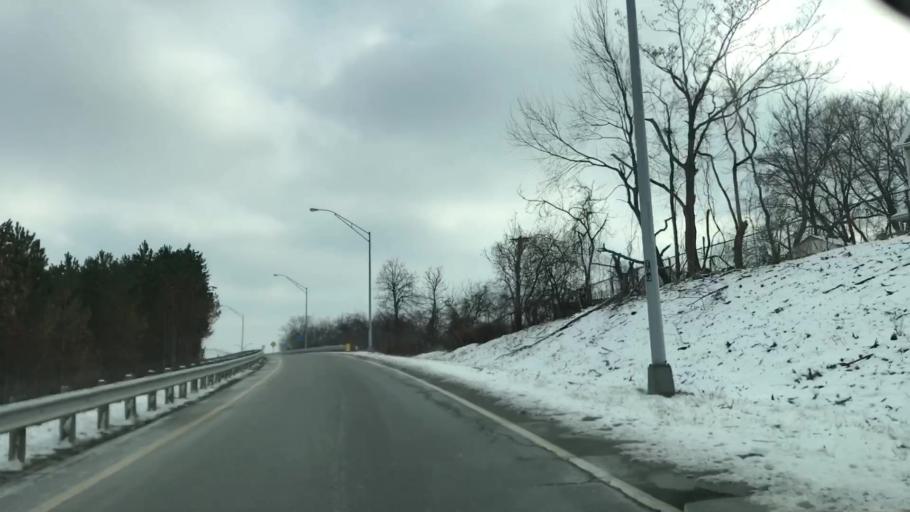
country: US
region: Ohio
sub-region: Mahoning County
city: Youngstown
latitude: 41.0917
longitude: -80.6534
